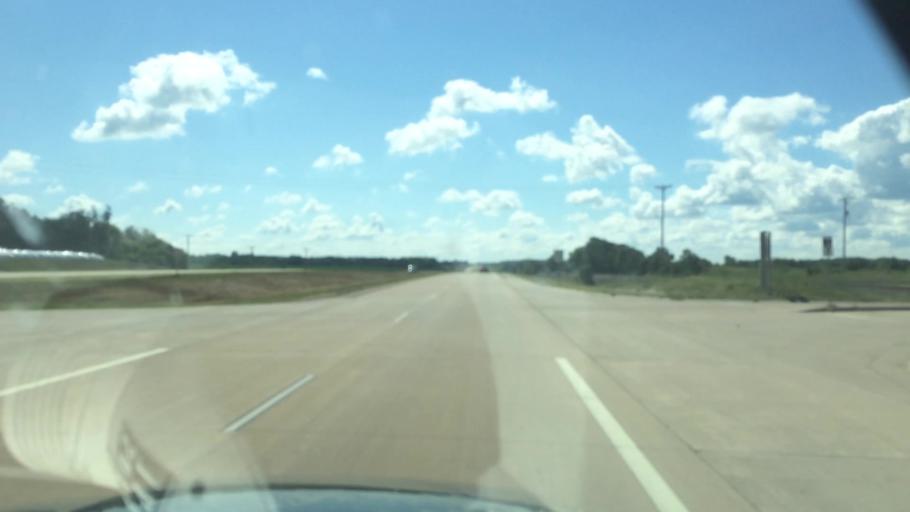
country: US
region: Wisconsin
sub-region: Portage County
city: Amherst
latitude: 44.4942
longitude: -89.3664
